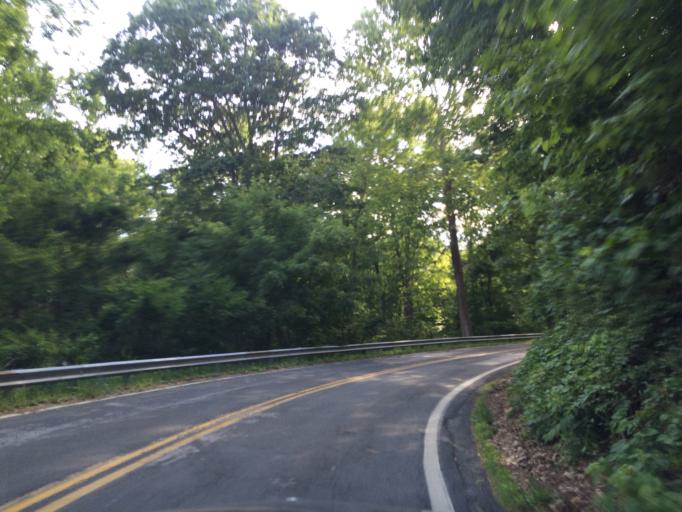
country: US
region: Maryland
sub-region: Carroll County
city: Eldersburg
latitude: 39.4856
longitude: -76.9850
